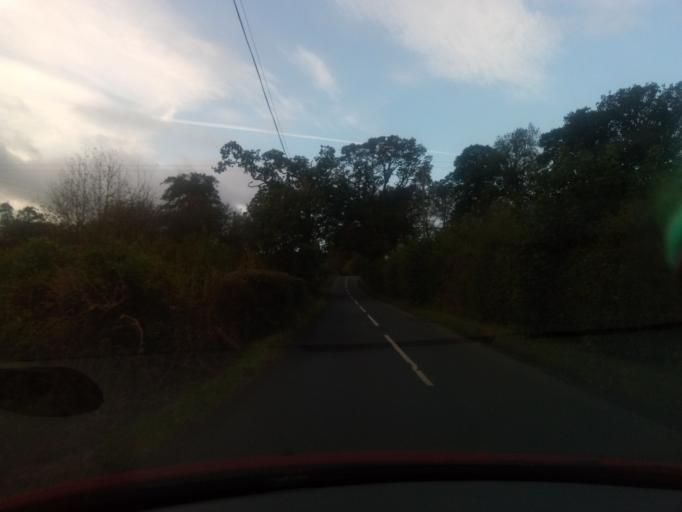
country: GB
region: Scotland
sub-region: The Scottish Borders
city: Jedburgh
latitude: 55.4123
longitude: -2.6462
